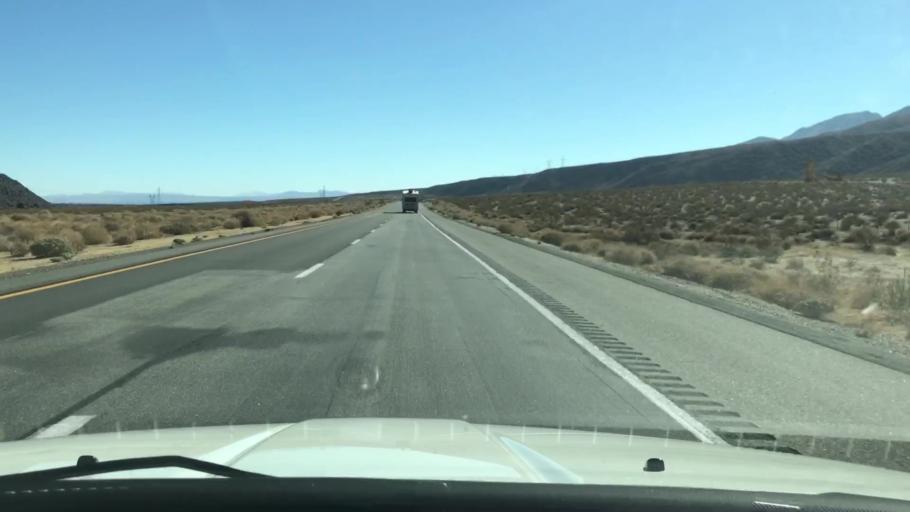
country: US
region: California
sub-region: Kern County
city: Inyokern
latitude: 35.9019
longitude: -117.9005
